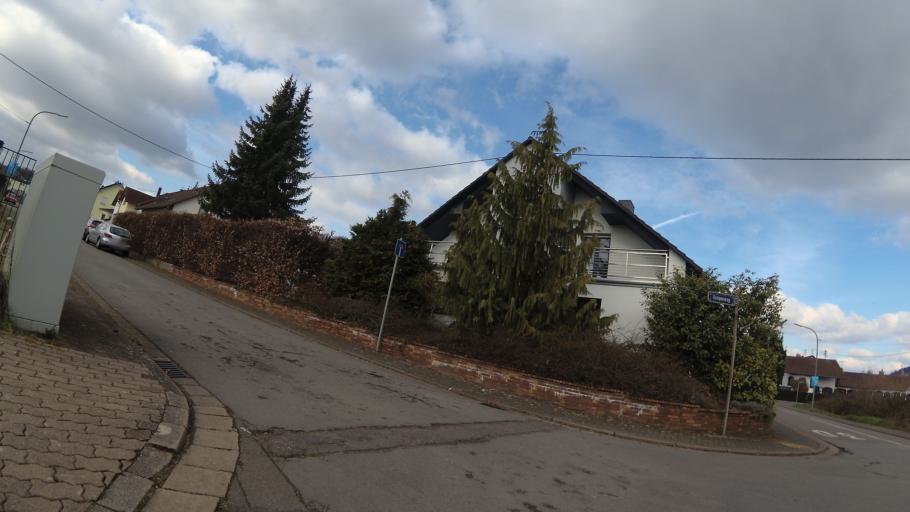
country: DE
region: Saarland
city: Rehlingen-Siersburg
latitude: 49.3798
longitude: 6.6799
